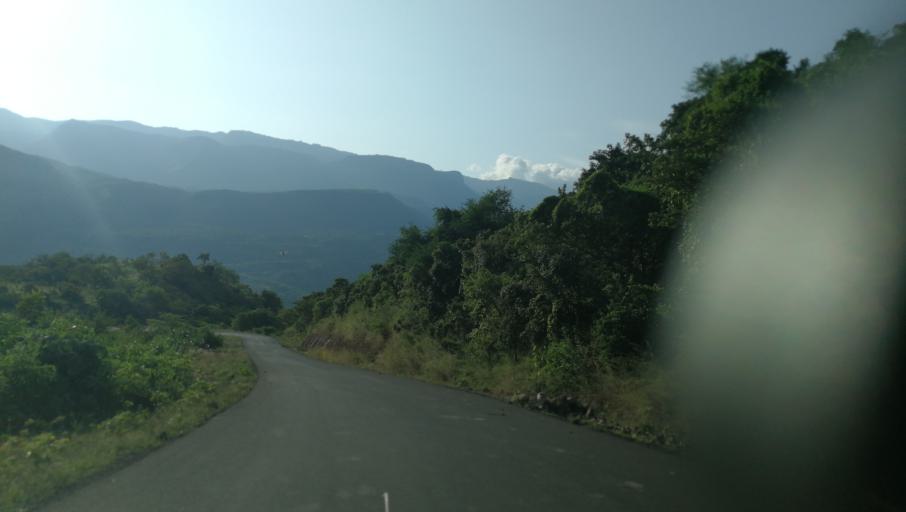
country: ET
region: Southern Nations, Nationalities, and People's Region
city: Areka
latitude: 6.8251
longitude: 37.3031
